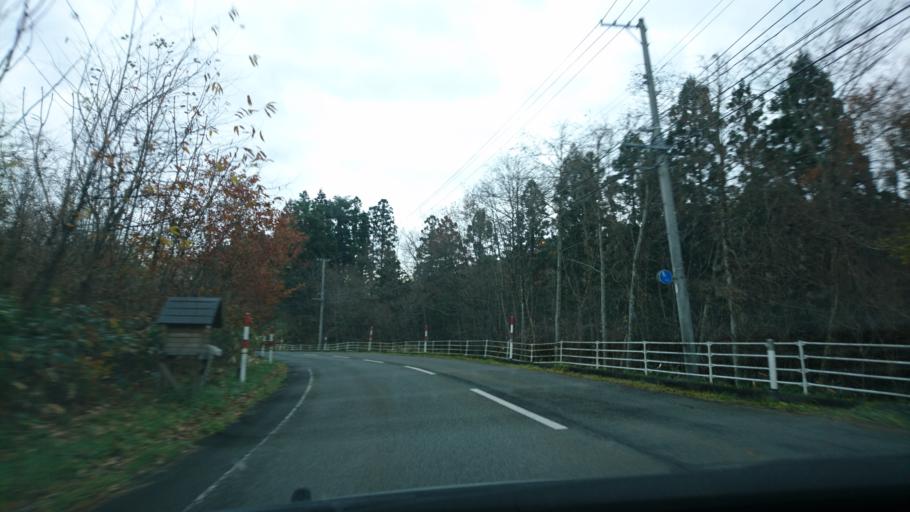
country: JP
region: Iwate
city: Ichinoseki
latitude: 38.9643
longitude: 140.9393
